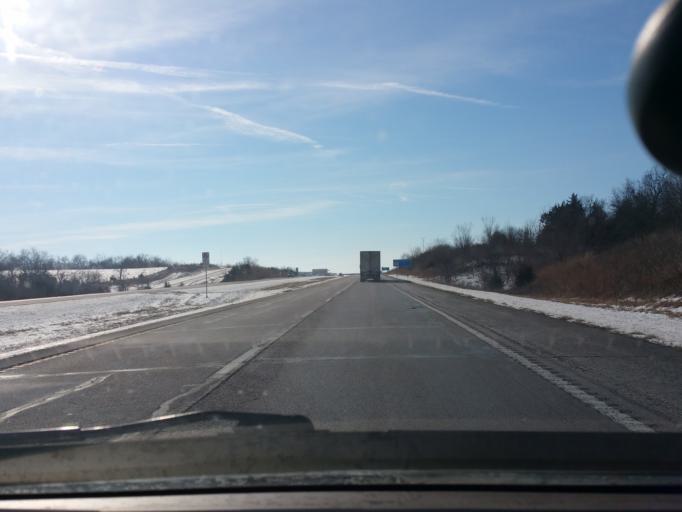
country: US
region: Iowa
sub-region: Decatur County
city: Lamoni
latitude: 40.4792
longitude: -93.9736
